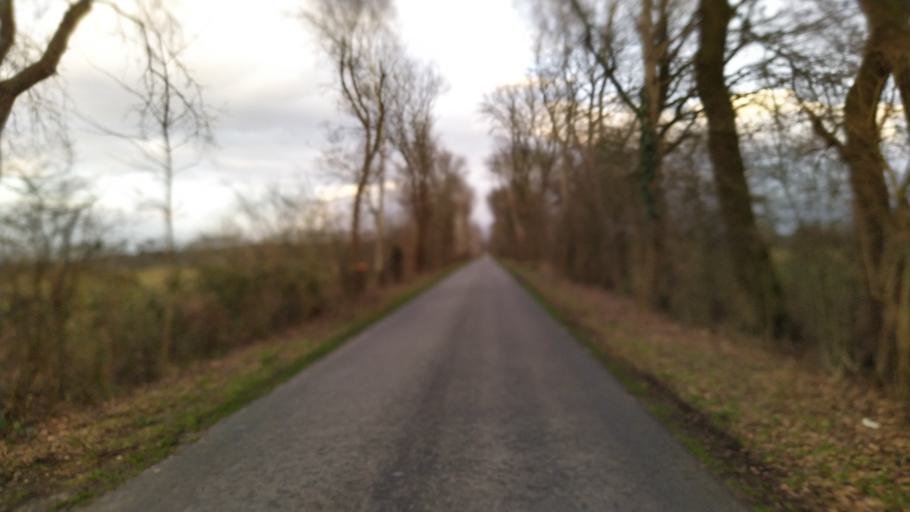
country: DE
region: Lower Saxony
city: Harsefeld
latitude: 53.4336
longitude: 9.4750
